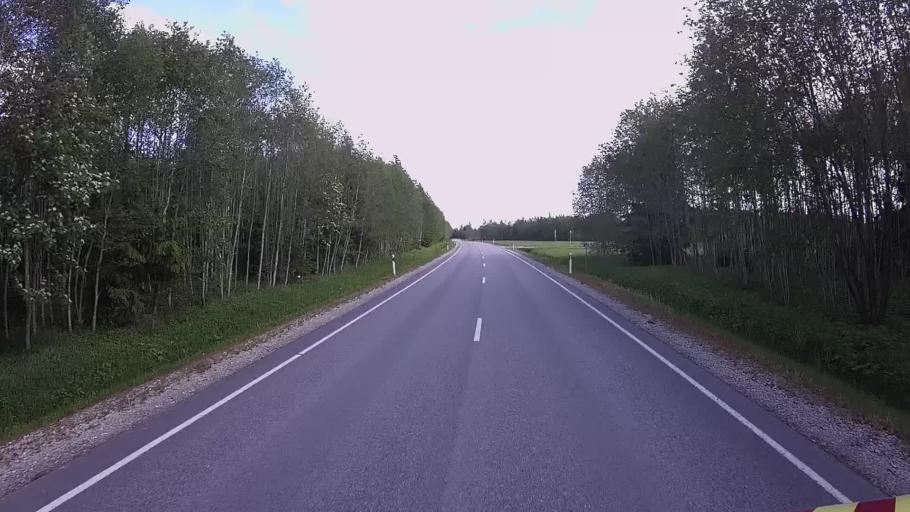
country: EE
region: Jogevamaa
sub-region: Mustvee linn
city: Mustvee
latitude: 58.8804
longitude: 26.8163
